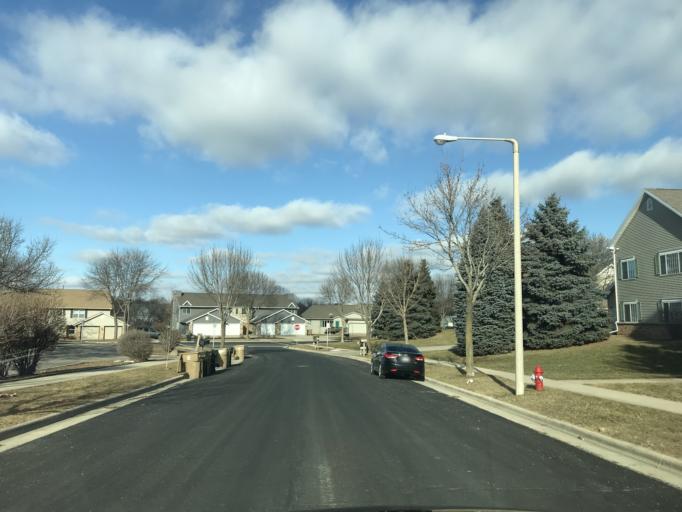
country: US
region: Wisconsin
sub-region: Dane County
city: Monona
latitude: 43.1115
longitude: -89.2979
